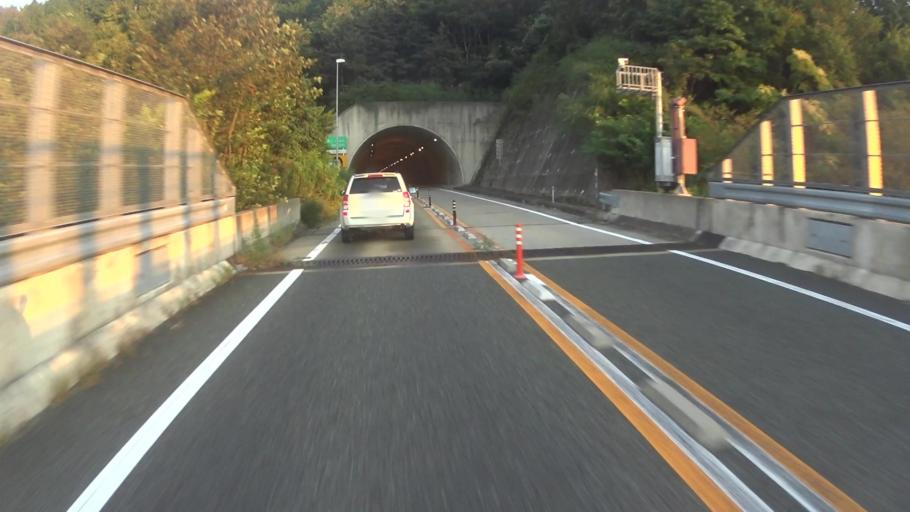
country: JP
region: Kyoto
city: Ayabe
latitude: 35.3495
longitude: 135.2919
